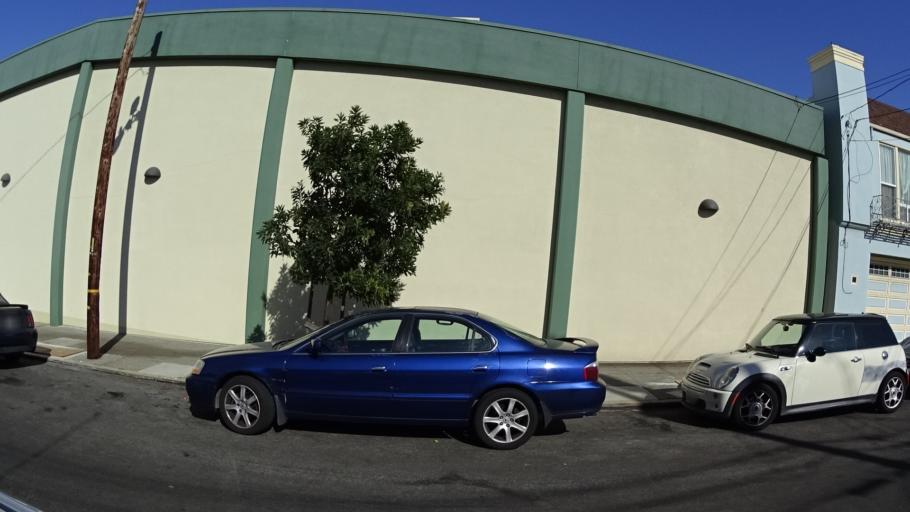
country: US
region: California
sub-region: San Francisco County
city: San Francisco
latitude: 37.7308
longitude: -122.4093
